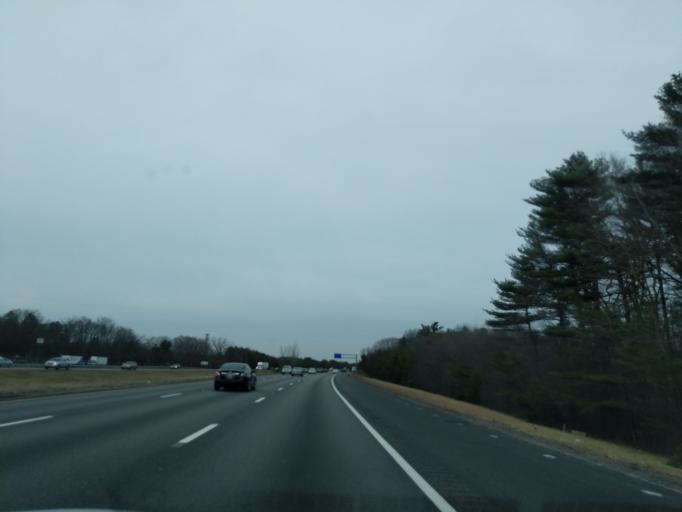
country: US
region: Massachusetts
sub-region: Norfolk County
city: Plainville
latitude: 42.0005
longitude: -71.2896
